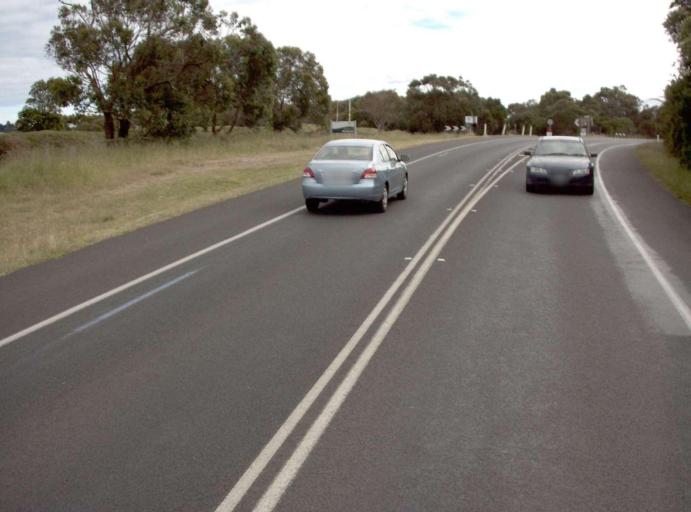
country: AU
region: Victoria
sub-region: Bass Coast
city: Phillip Island
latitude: -38.5173
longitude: 145.3424
